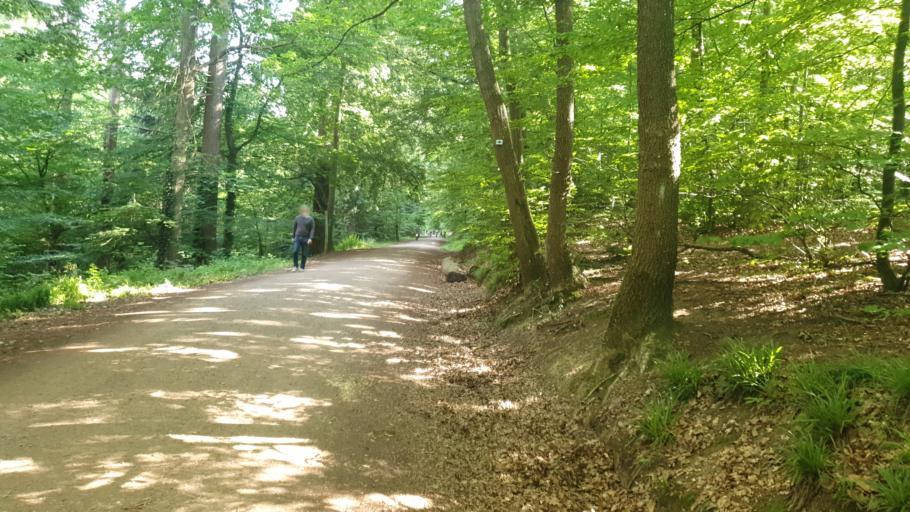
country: DE
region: Baden-Wuerttemberg
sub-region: Freiburg Region
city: Merzhausen
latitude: 47.9706
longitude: 7.8377
